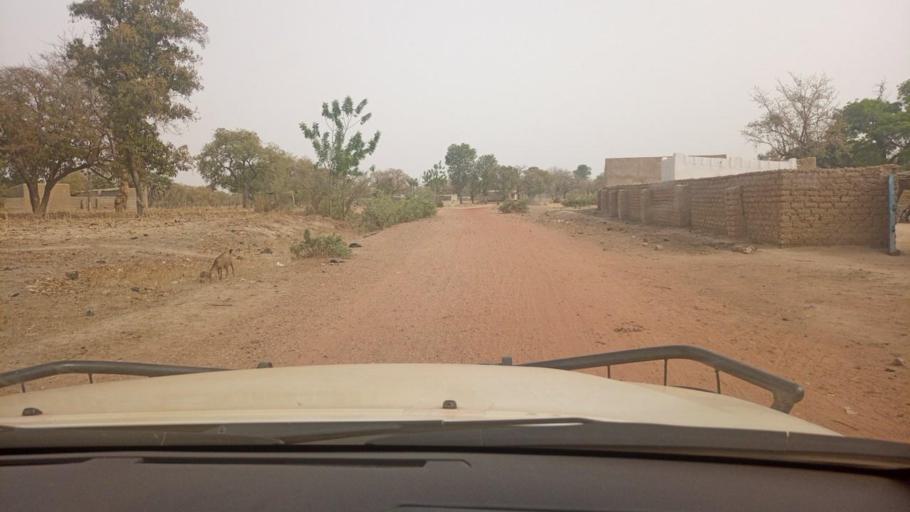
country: BF
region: Boucle du Mouhoun
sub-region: Province des Banwa
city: Salanso
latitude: 12.1126
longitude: -4.3374
